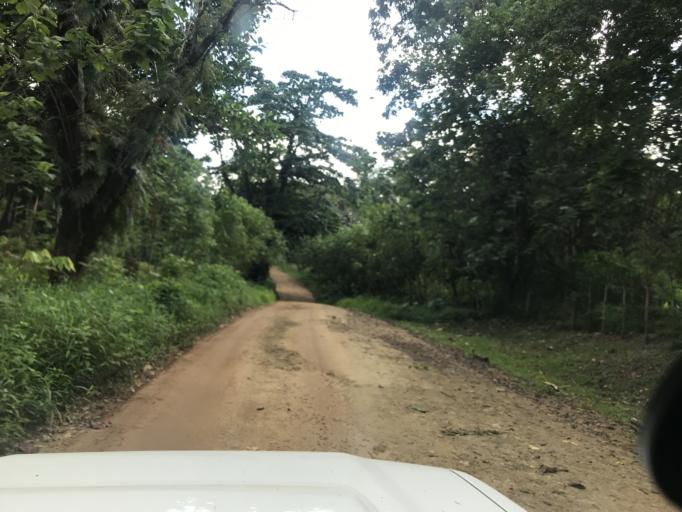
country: VU
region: Sanma
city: Luganville
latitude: -15.4900
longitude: 167.0898
